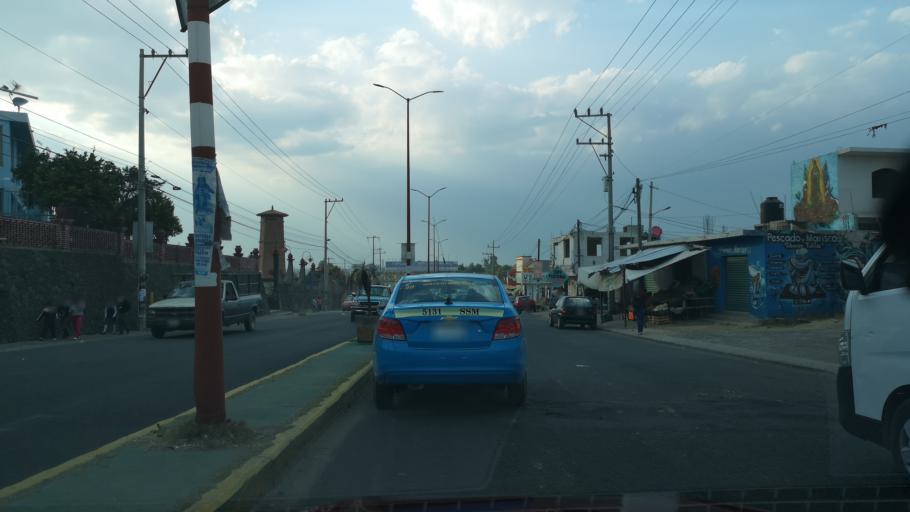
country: MX
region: Puebla
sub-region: Juan C. Bonilla
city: Santa Maria Zacatepec
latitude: 19.1222
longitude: -98.3647
